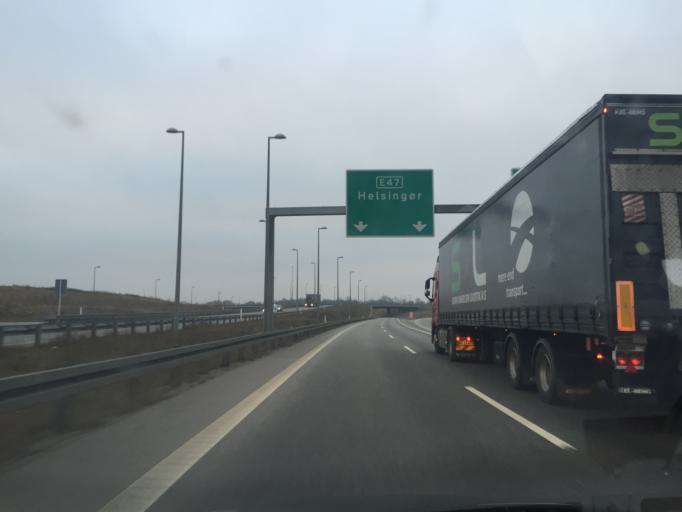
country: DK
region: Capital Region
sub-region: Glostrup Kommune
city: Glostrup
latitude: 55.6911
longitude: 12.4226
